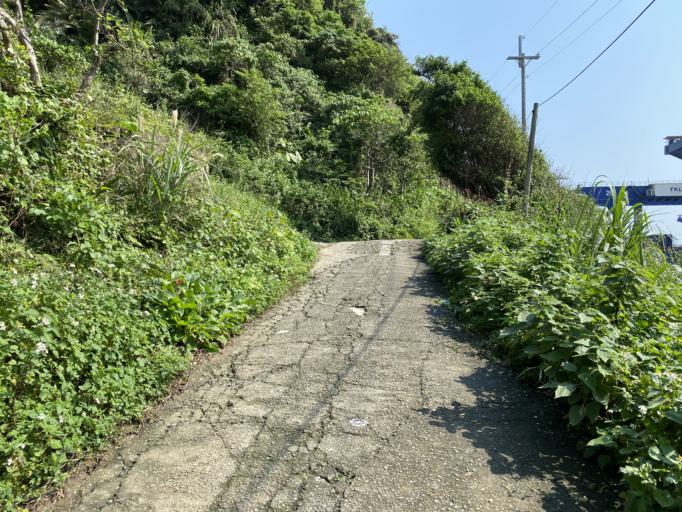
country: TW
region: Taiwan
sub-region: Keelung
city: Keelung
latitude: 25.1541
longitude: 121.7465
